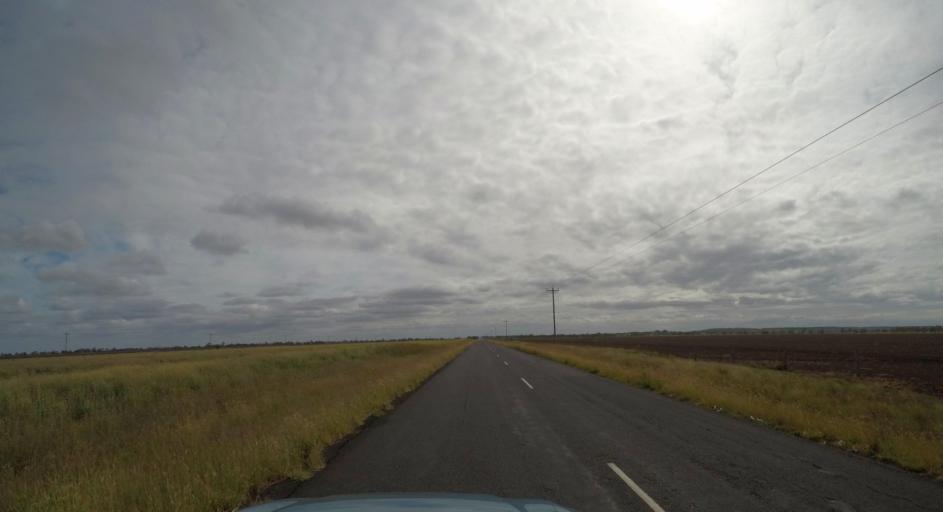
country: AU
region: Queensland
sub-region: Western Downs
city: Dalby
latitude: -26.9995
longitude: 151.2325
